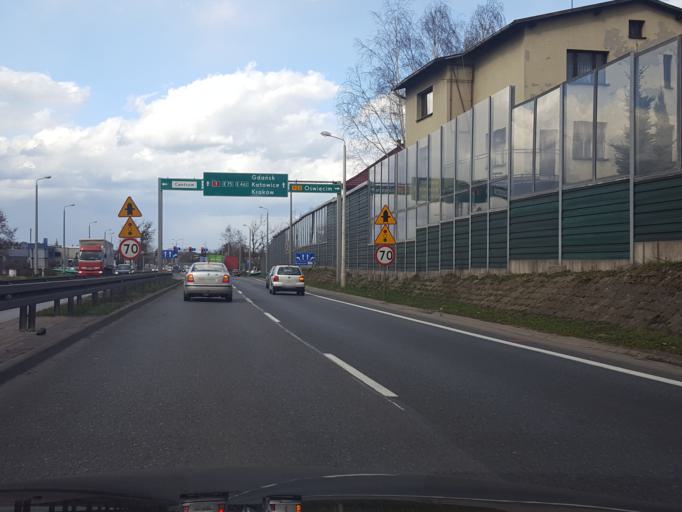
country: PL
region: Silesian Voivodeship
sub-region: Powiat pszczynski
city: Pszczyna
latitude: 49.9740
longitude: 18.9584
